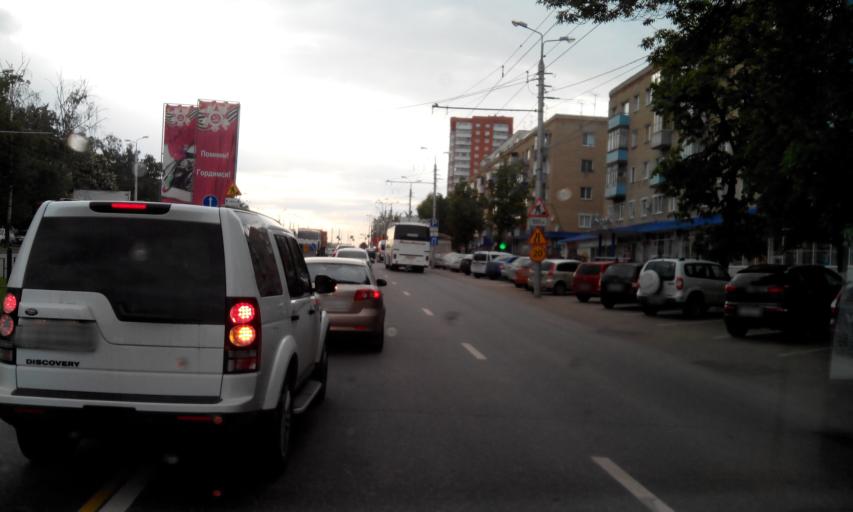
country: RU
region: Penza
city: Penza
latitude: 53.2164
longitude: 44.9825
